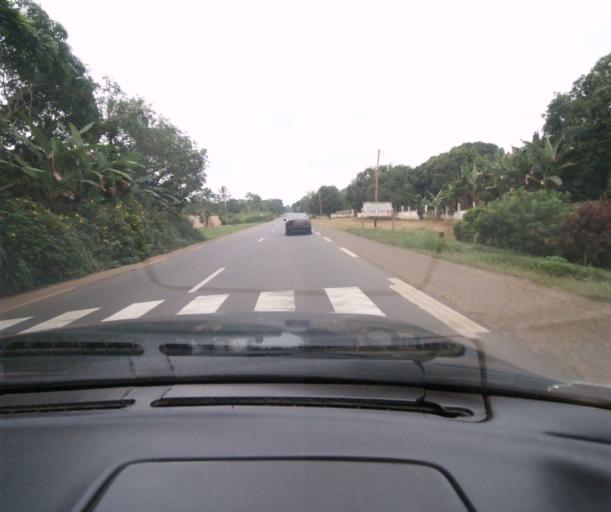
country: CM
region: Centre
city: Obala
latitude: 4.1693
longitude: 11.4826
